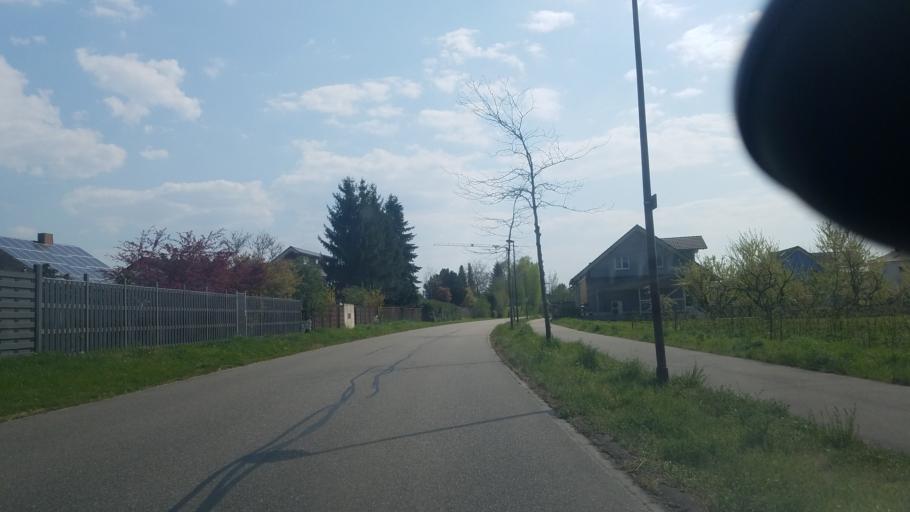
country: DE
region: Baden-Wuerttemberg
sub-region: Freiburg Region
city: Achern
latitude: 48.6338
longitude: 8.0442
